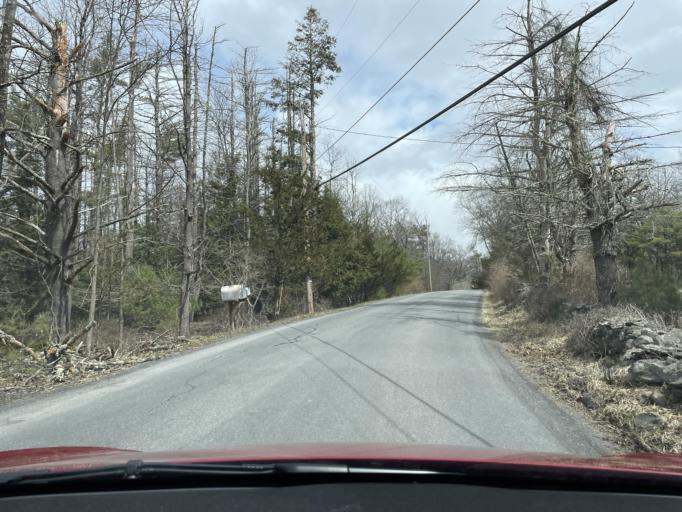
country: US
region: New York
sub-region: Ulster County
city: Zena
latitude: 42.0331
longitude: -74.0390
